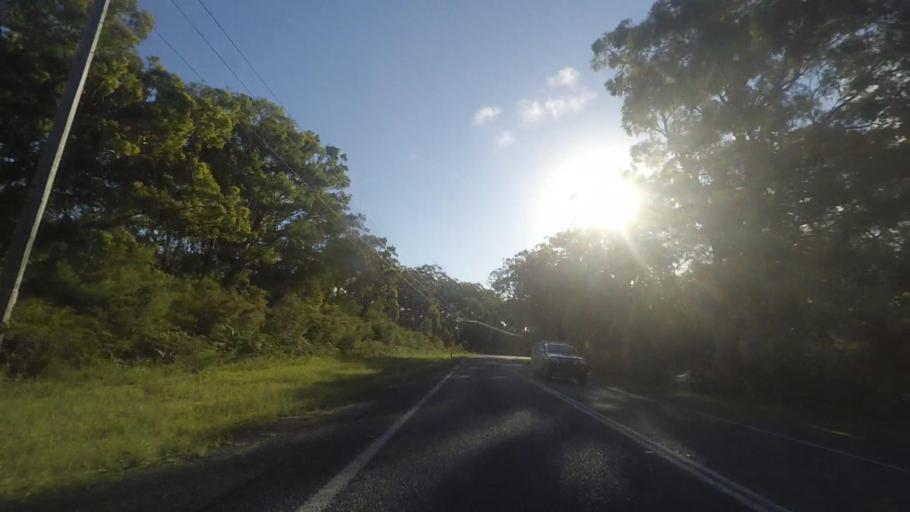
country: AU
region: New South Wales
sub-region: Great Lakes
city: Nabiac
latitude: -32.0901
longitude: 152.4615
